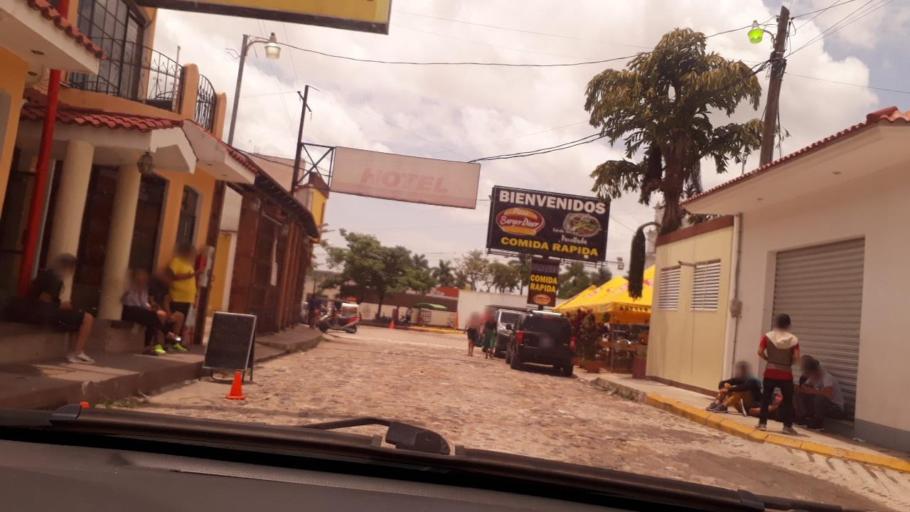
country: GT
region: Chiquimula
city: Esquipulas
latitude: 14.5608
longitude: -89.3524
